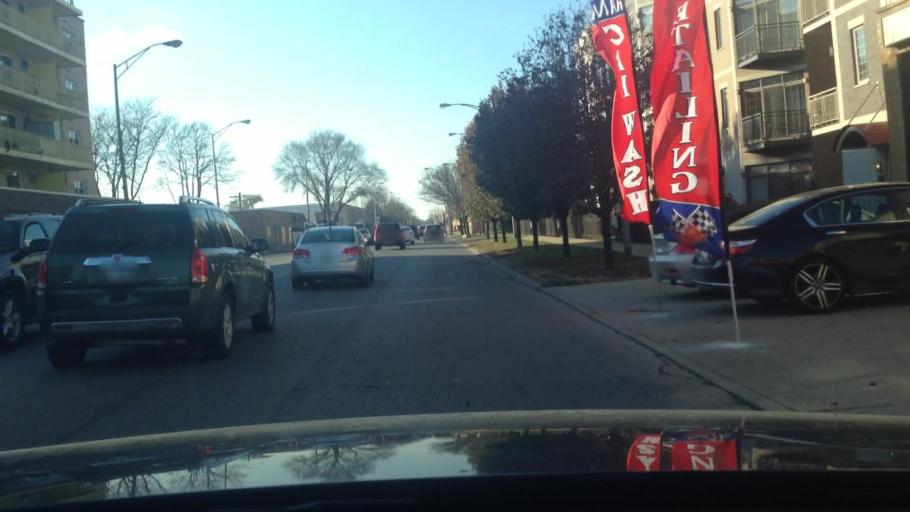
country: US
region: Illinois
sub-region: Cook County
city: River Grove
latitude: 41.9269
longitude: -87.8242
